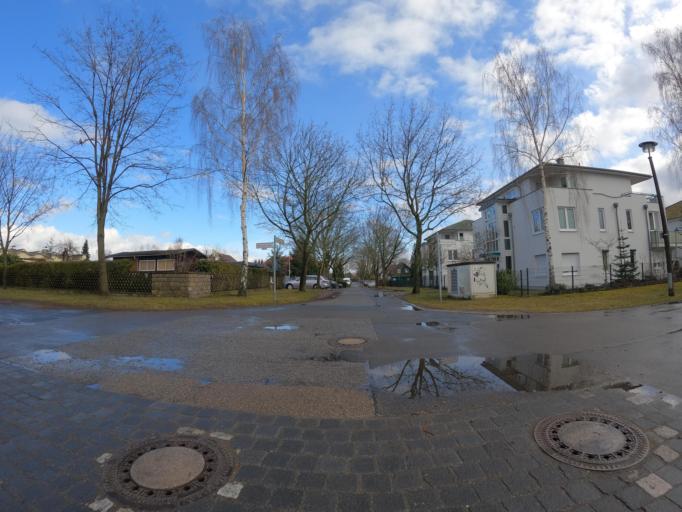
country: DE
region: Berlin
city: Marzahn
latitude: 52.5327
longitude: 13.5621
